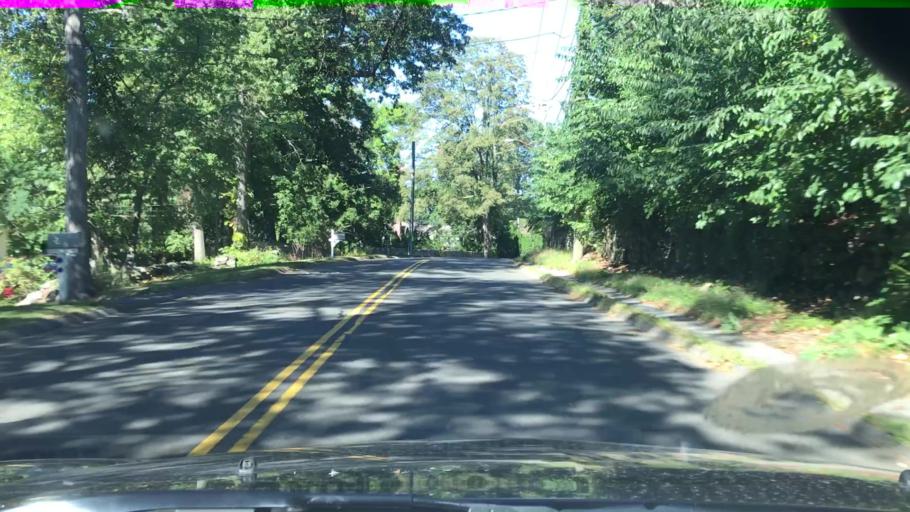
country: US
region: Connecticut
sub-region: Fairfield County
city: Darien
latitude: 41.0801
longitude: -73.4446
